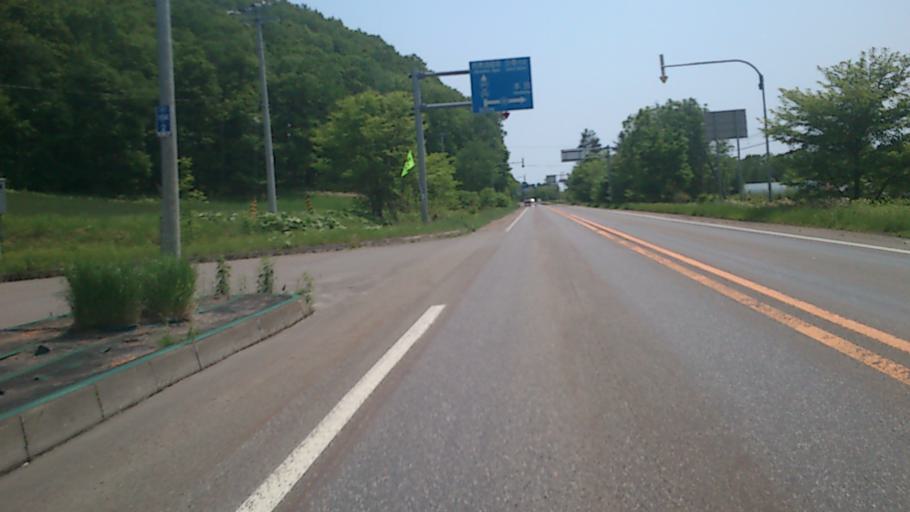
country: JP
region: Hokkaido
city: Otofuke
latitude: 43.2428
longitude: 143.4848
